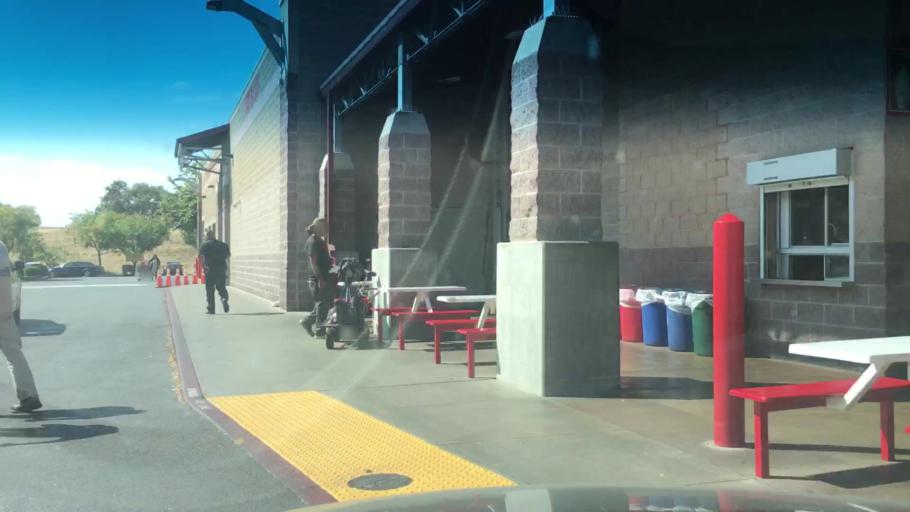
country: US
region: California
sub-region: Sacramento County
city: Sacramento
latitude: 38.5974
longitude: -121.4525
